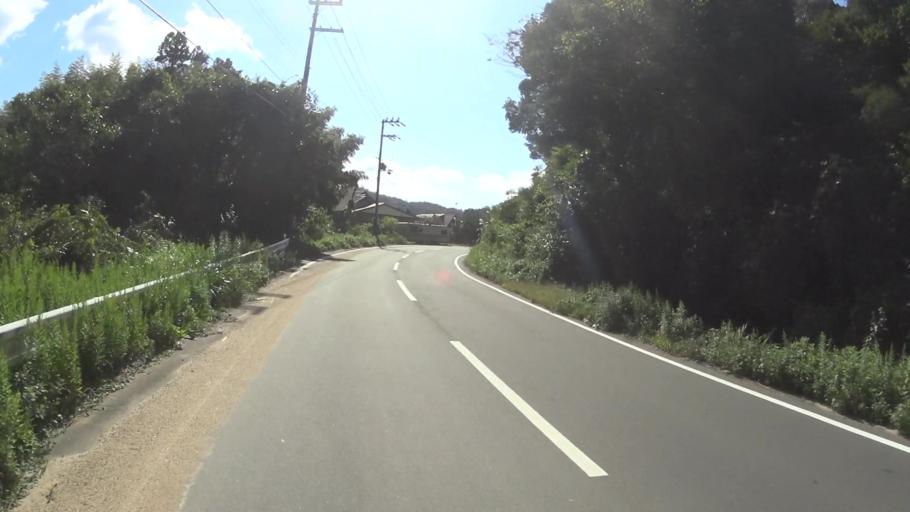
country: JP
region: Kyoto
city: Miyazu
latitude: 35.6981
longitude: 135.1013
